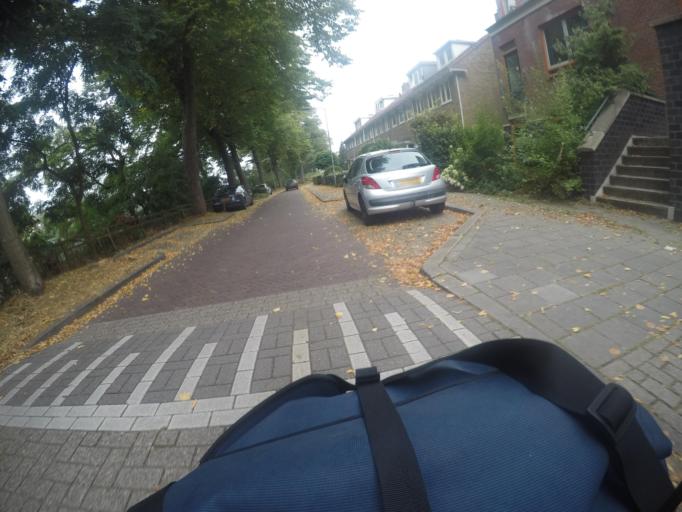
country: NL
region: Gelderland
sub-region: Gemeente Arnhem
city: Burgemeesterswijk
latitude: 51.9864
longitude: 5.8935
